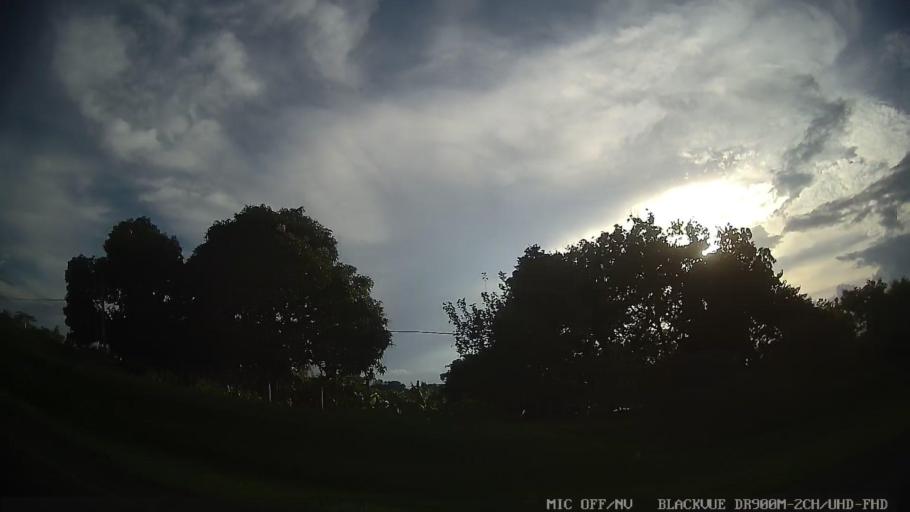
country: BR
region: Sao Paulo
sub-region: Tiete
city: Tiete
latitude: -23.1528
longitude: -47.6617
